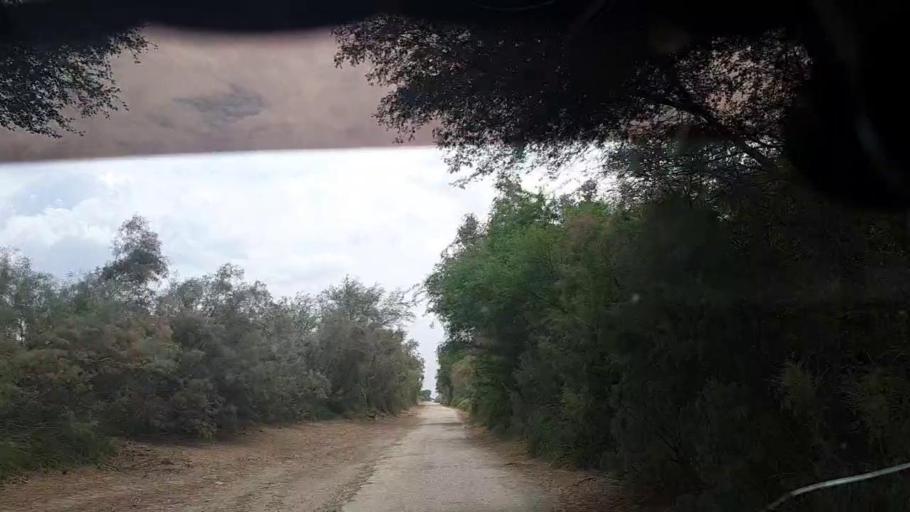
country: PK
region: Sindh
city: Rustam jo Goth
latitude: 28.0395
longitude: 68.9398
